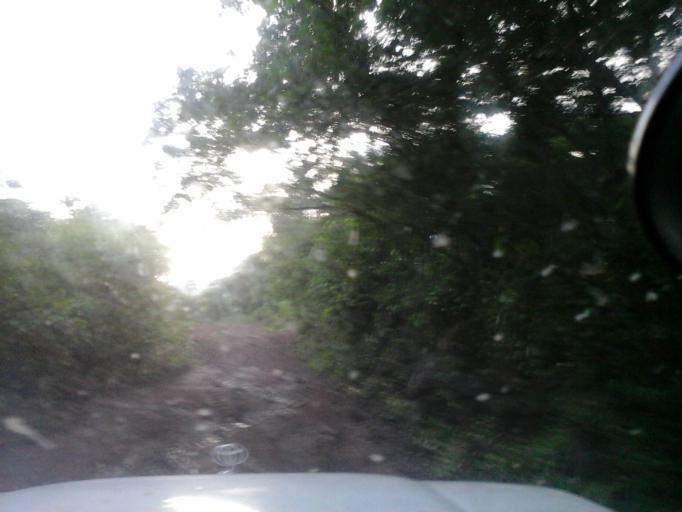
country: CO
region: Cesar
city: Agustin Codazzi
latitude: 10.1710
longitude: -73.1693
